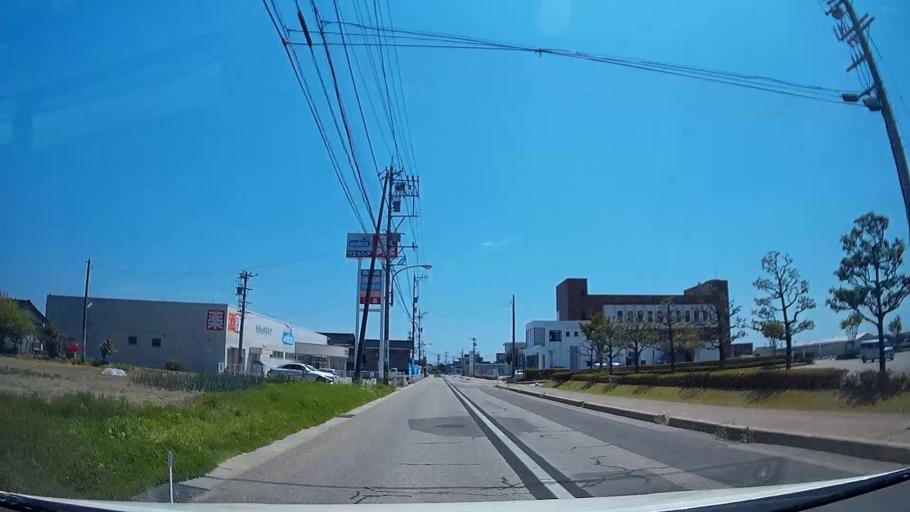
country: JP
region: Ishikawa
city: Nanao
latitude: 37.4438
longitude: 137.2725
